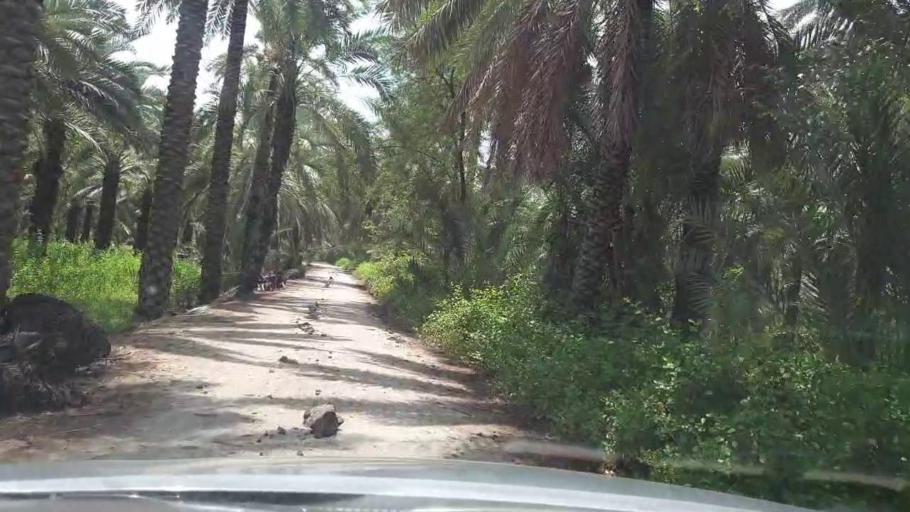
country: PK
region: Sindh
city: Khairpur
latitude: 27.6355
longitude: 68.7301
